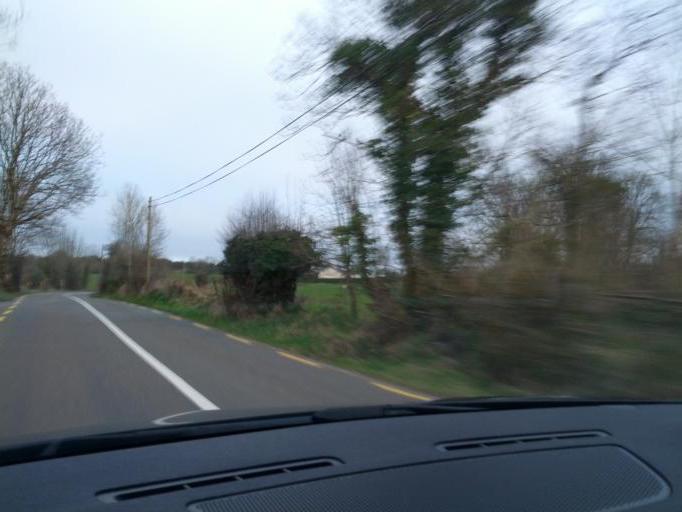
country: IE
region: Connaught
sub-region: Sligo
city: Ballymote
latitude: 54.0098
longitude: -8.5477
